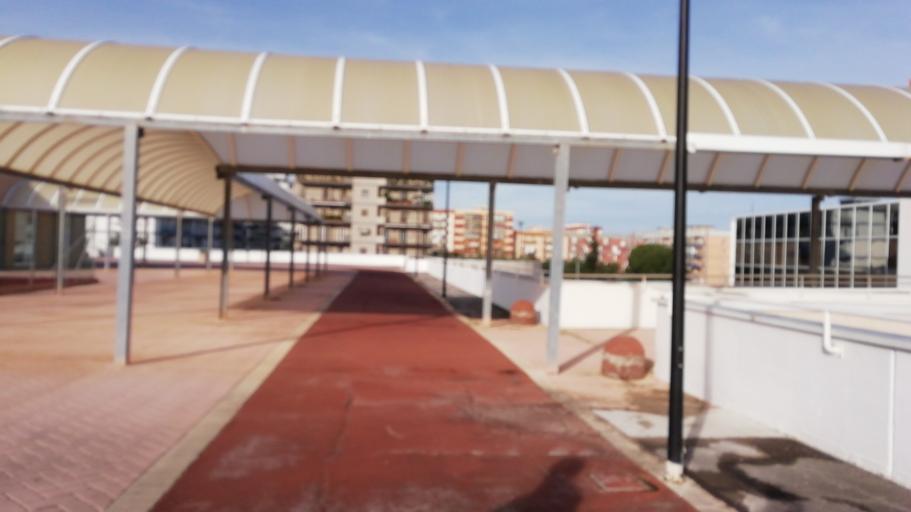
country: IT
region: Apulia
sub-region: Provincia di Bari
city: Triggiano
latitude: 41.1057
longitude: 16.9120
